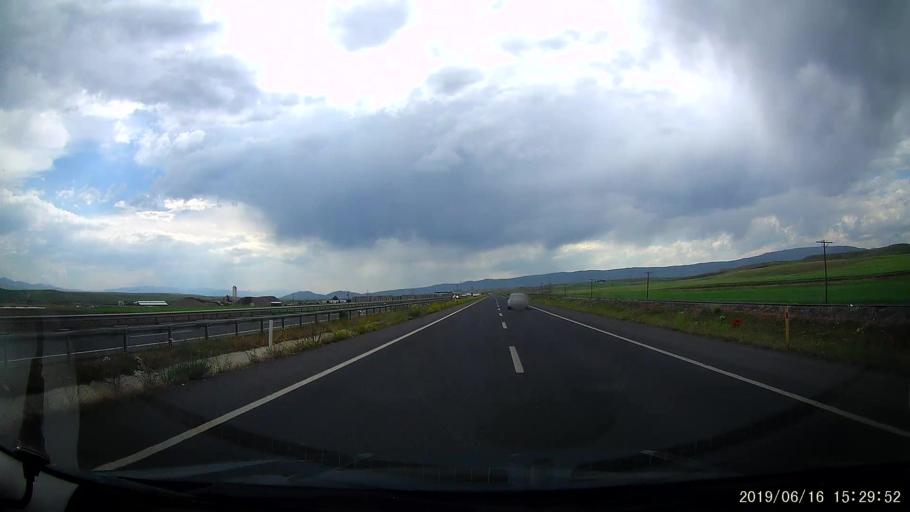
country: TR
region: Erzurum
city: Horasan
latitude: 40.0326
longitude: 42.1208
